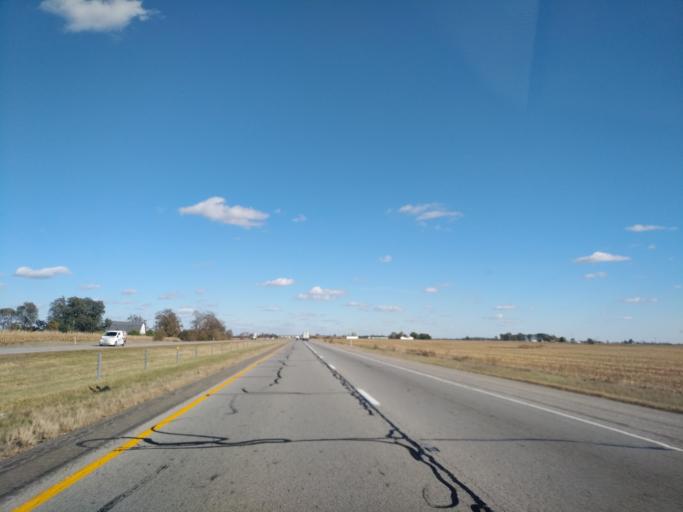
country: US
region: Indiana
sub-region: Hancock County
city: Greenfield
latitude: 39.8257
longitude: -85.6582
